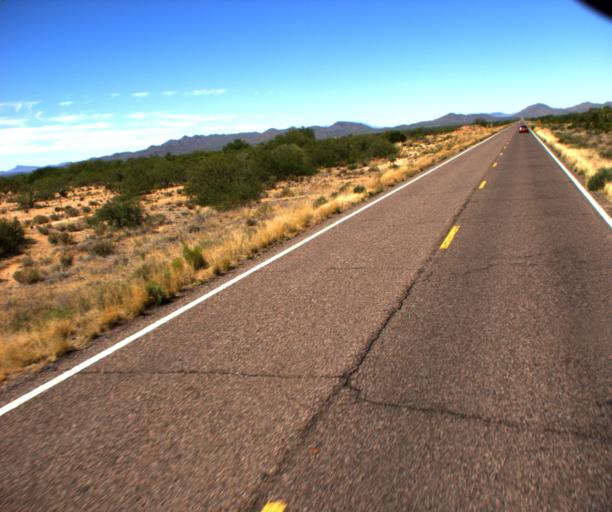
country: US
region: Arizona
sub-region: Yavapai County
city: Congress
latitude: 34.1467
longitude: -112.8919
